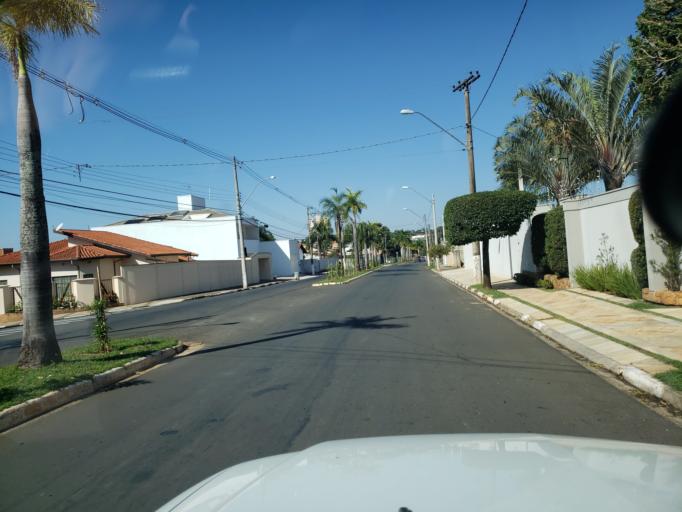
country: BR
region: Sao Paulo
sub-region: Itapira
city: Itapira
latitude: -22.4265
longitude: -46.8367
